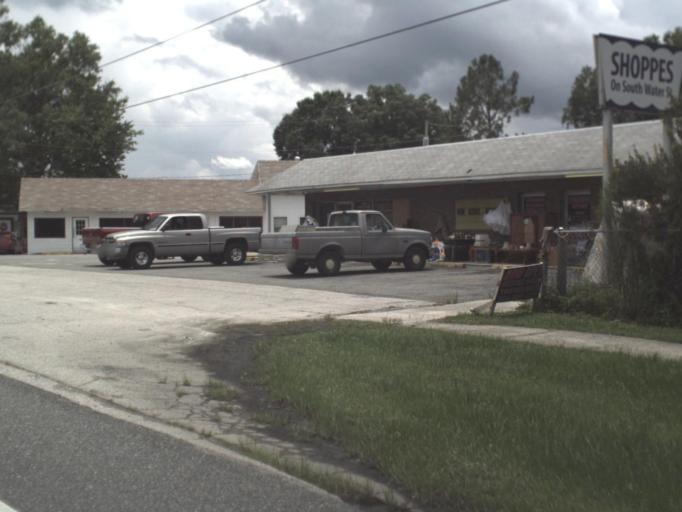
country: US
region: Florida
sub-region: Bradford County
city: Starke
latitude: 29.9351
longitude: -82.1051
